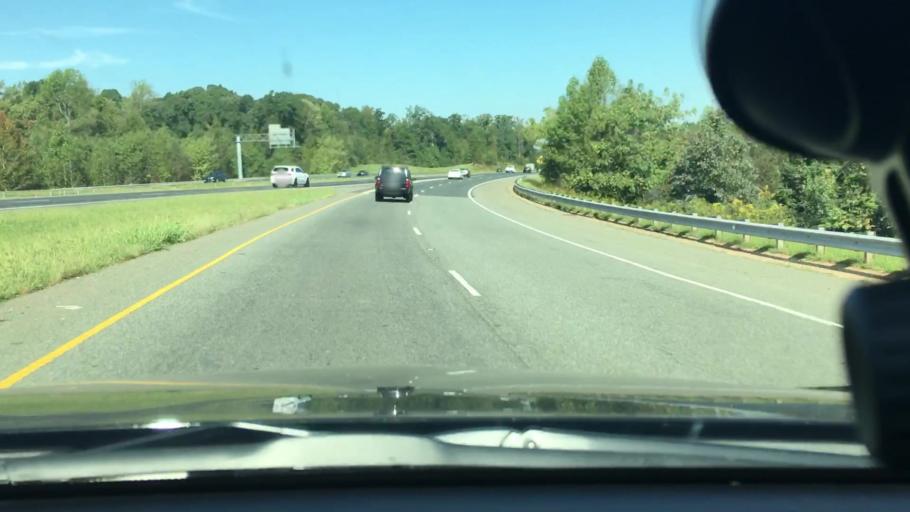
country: US
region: North Carolina
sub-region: Mecklenburg County
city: Mint Hill
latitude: 35.2236
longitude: -80.6513
